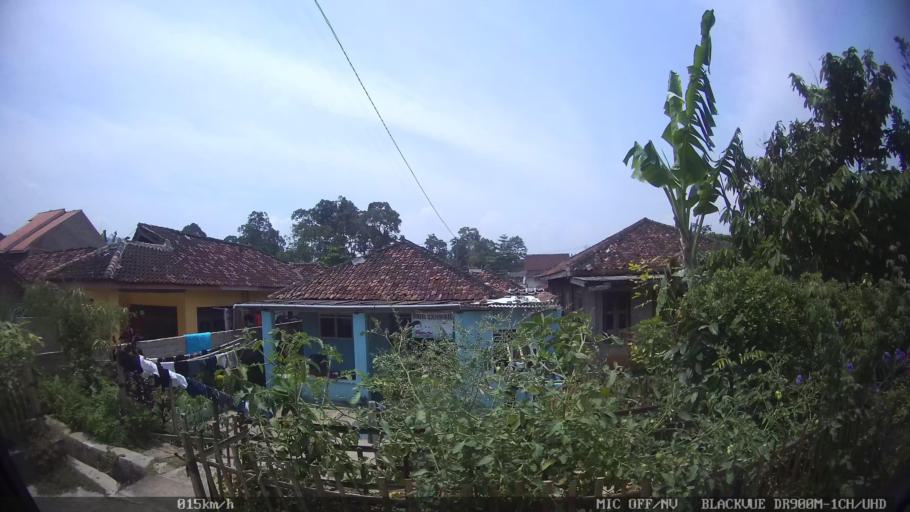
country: ID
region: Lampung
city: Bandarlampung
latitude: -5.4392
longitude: 105.2387
